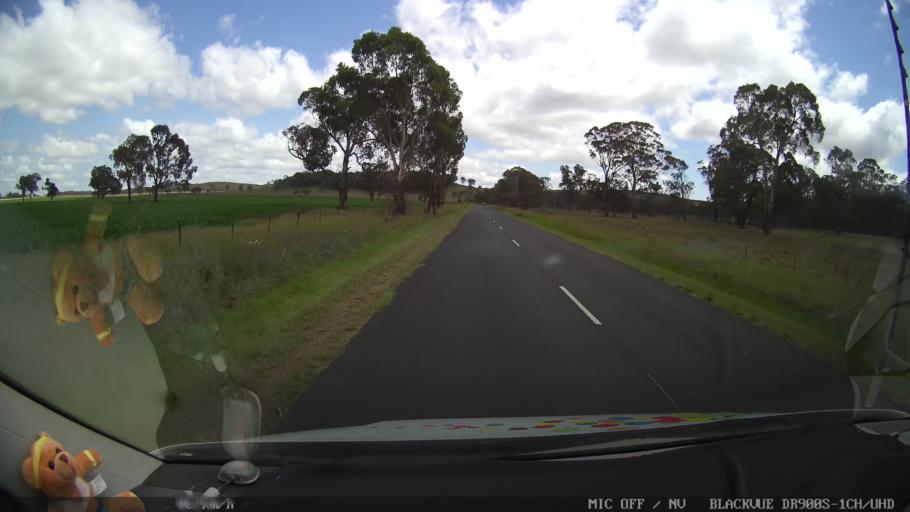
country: AU
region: New South Wales
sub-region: Glen Innes Severn
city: Glen Innes
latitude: -29.6007
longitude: 151.6665
